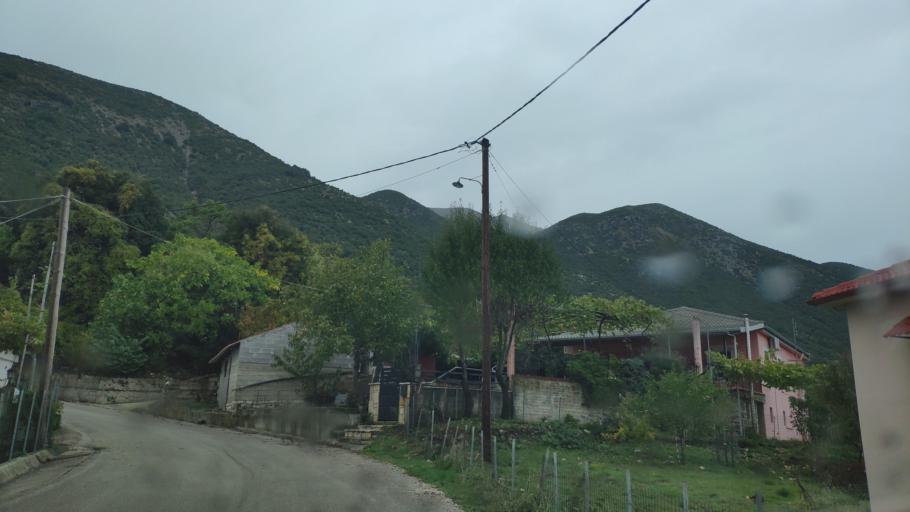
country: GR
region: Epirus
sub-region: Nomos Thesprotias
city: Paramythia
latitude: 39.4603
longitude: 20.6703
